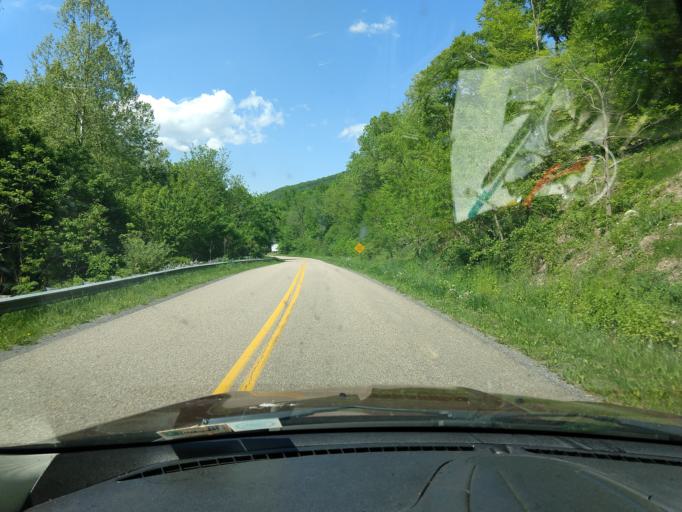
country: US
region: Virginia
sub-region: City of Covington
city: Fairlawn
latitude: 37.7314
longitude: -79.9144
